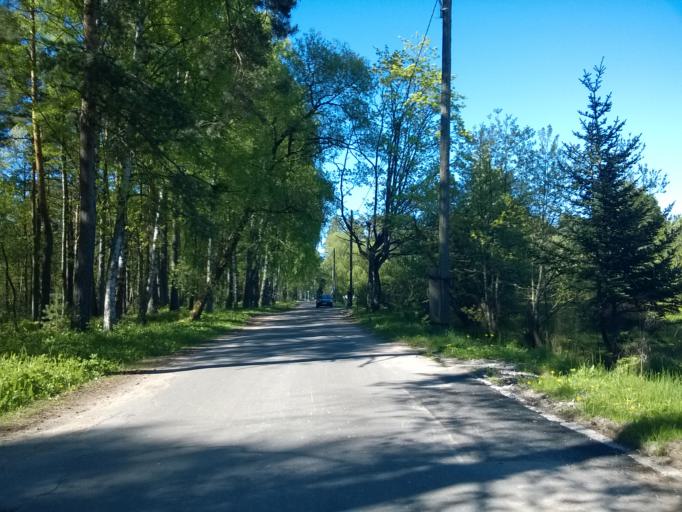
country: LV
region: Jurmala
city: Jurmala
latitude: 56.9565
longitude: 23.6666
